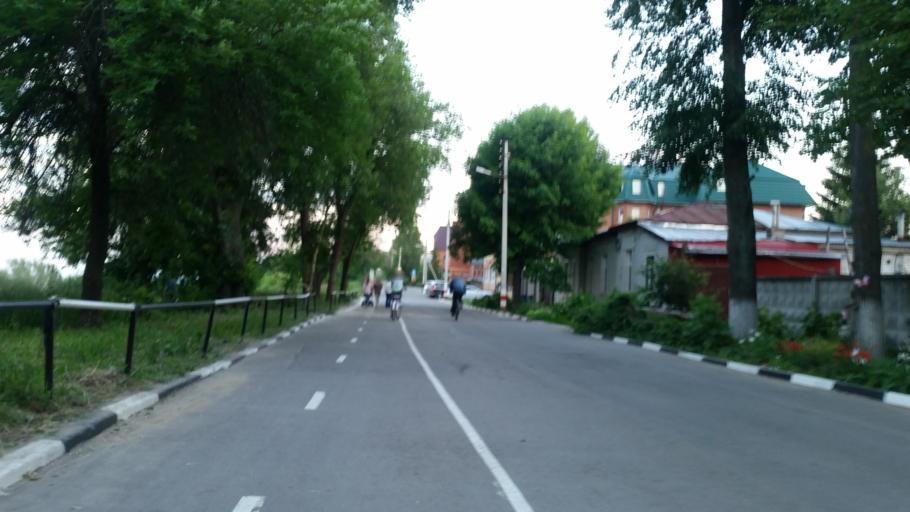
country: RU
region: Ulyanovsk
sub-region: Ulyanovskiy Rayon
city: Ulyanovsk
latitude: 54.3256
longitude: 48.4091
